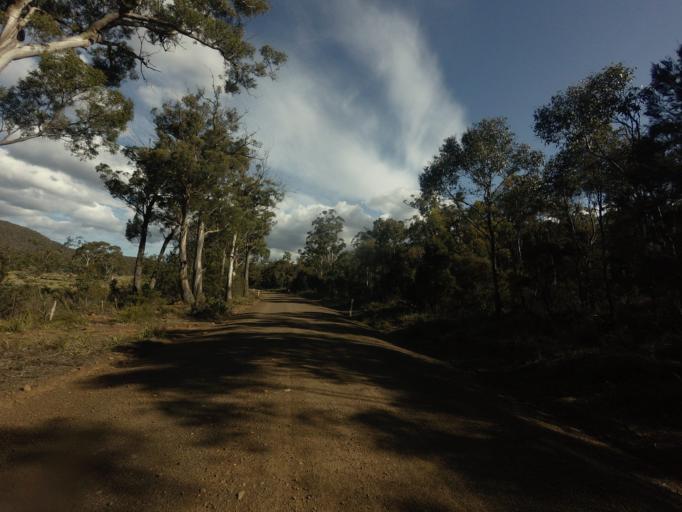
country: AU
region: Tasmania
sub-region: Break O'Day
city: St Helens
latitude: -41.8523
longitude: 148.0116
